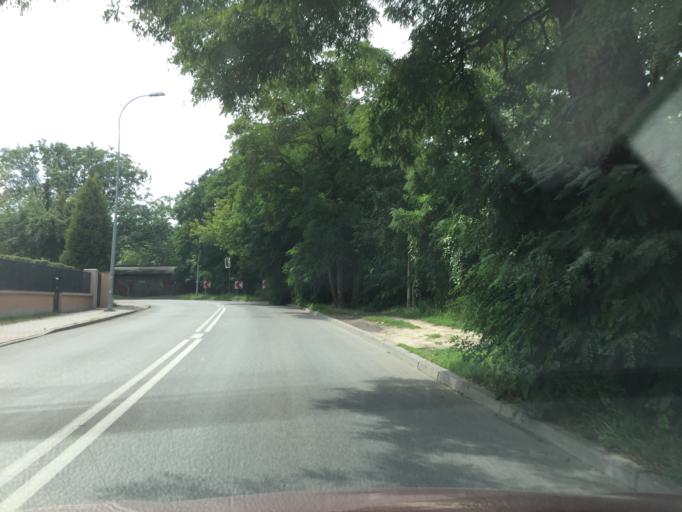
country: PL
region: Greater Poland Voivodeship
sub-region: Kalisz
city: Kalisz
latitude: 51.7436
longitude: 18.0754
